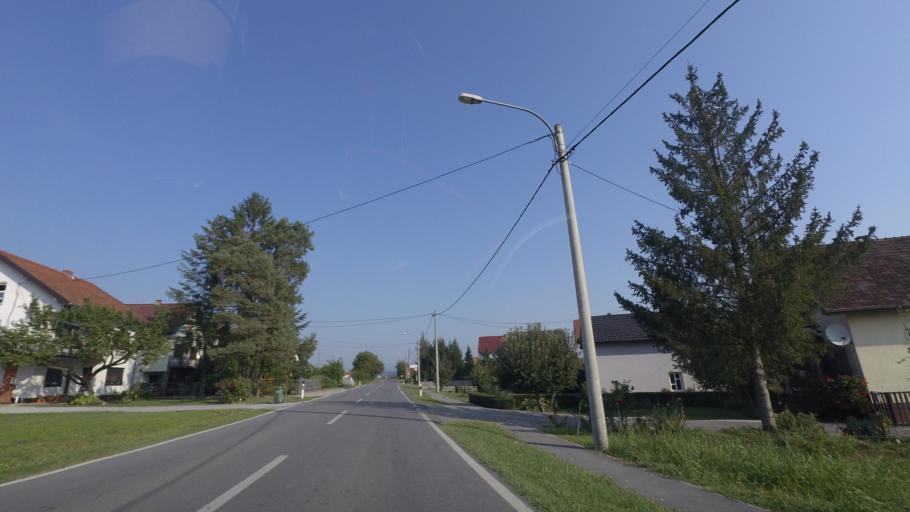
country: HR
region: Pozesko-Slavonska
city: Pozega
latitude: 45.3321
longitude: 17.5945
